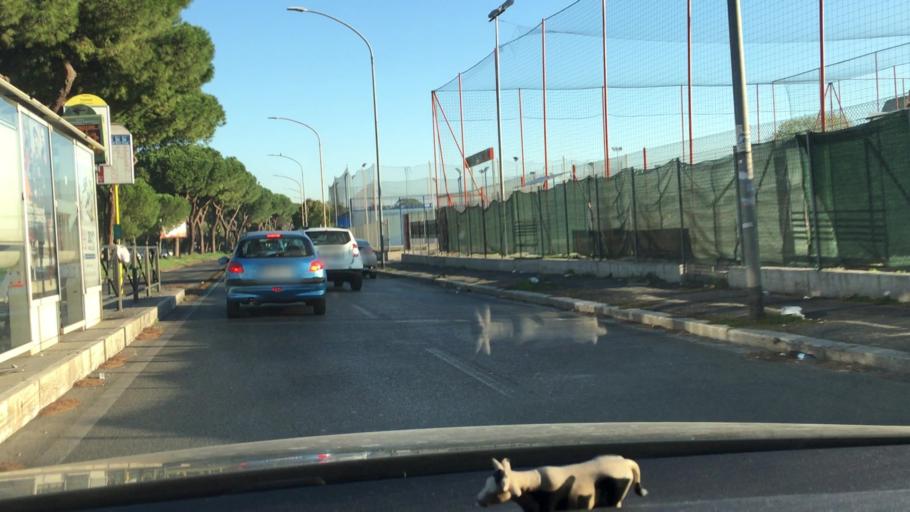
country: IT
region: Latium
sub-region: Citta metropolitana di Roma Capitale
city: Rome
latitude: 41.8704
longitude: 12.5685
